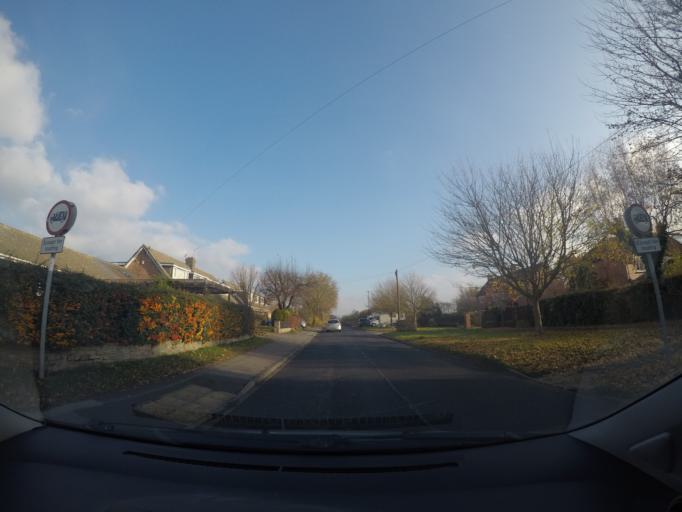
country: GB
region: England
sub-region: City of York
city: Huntington
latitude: 53.9986
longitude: -1.0537
